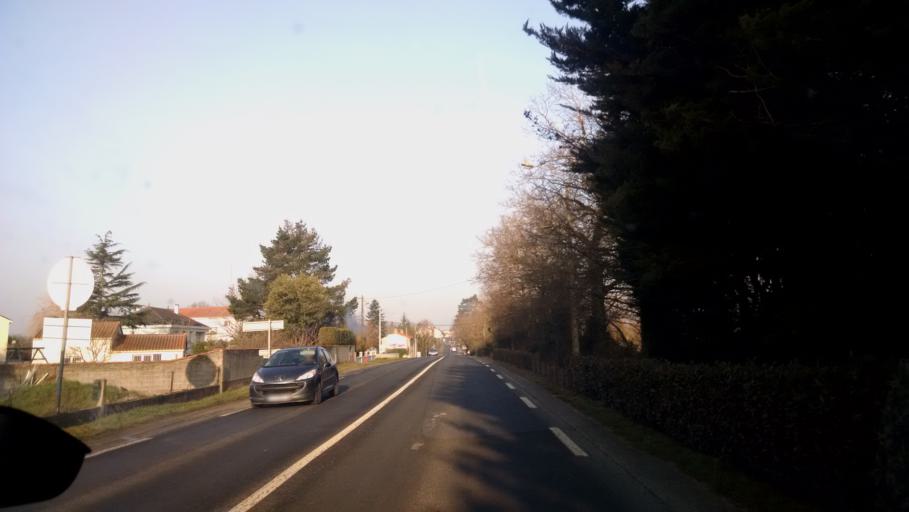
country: FR
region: Pays de la Loire
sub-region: Departement de la Loire-Atlantique
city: Aigrefeuille-sur-Maine
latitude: 47.0725
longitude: -1.3934
